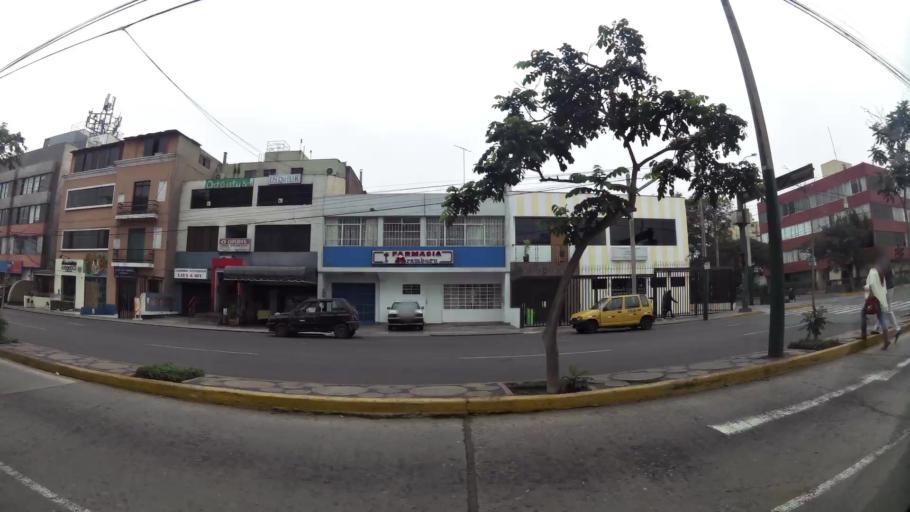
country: PE
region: Lima
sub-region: Lima
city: San Isidro
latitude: -12.1032
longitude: -77.0297
